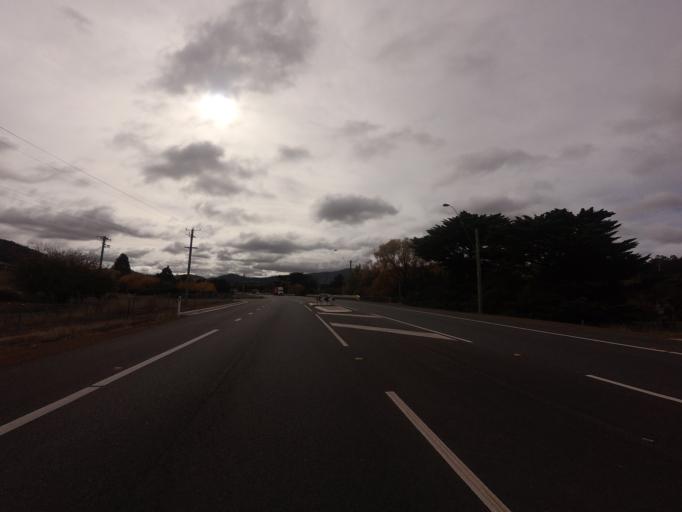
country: AU
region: Tasmania
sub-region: Brighton
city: Bridgewater
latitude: -42.6147
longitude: 147.2228
